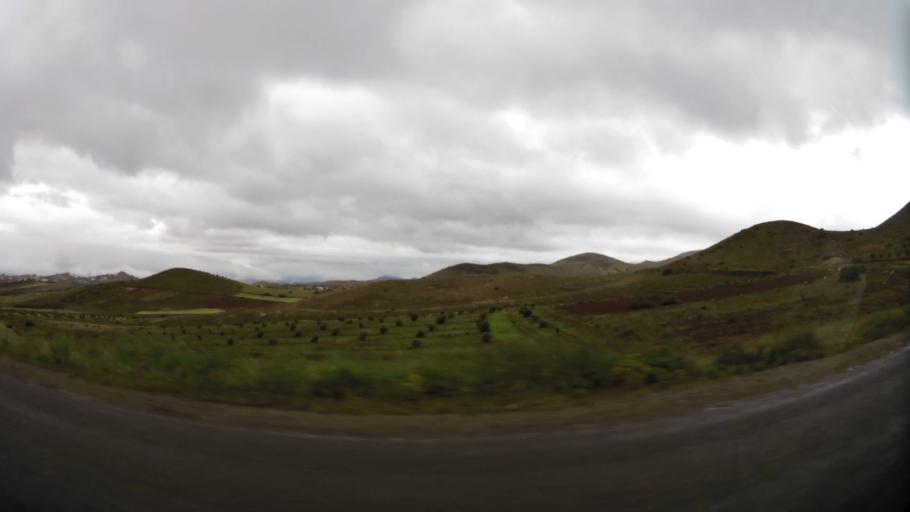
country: MA
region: Oriental
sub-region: Nador
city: Midar
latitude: 35.0665
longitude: -3.4748
